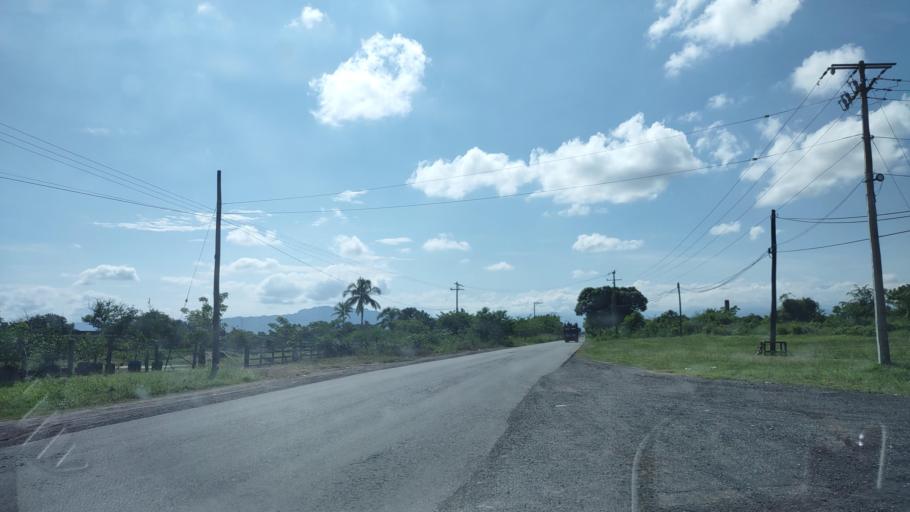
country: MX
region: Veracruz
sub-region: Martinez de la Torre
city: La Union Paso Largo
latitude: 20.1373
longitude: -96.9981
